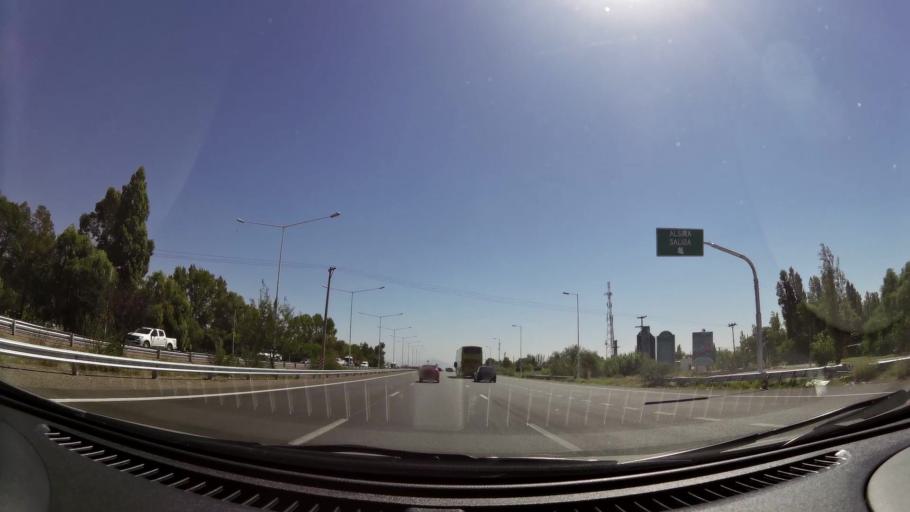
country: AR
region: Mendoza
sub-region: Departamento de Godoy Cruz
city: Godoy Cruz
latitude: -32.9212
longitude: -68.8239
